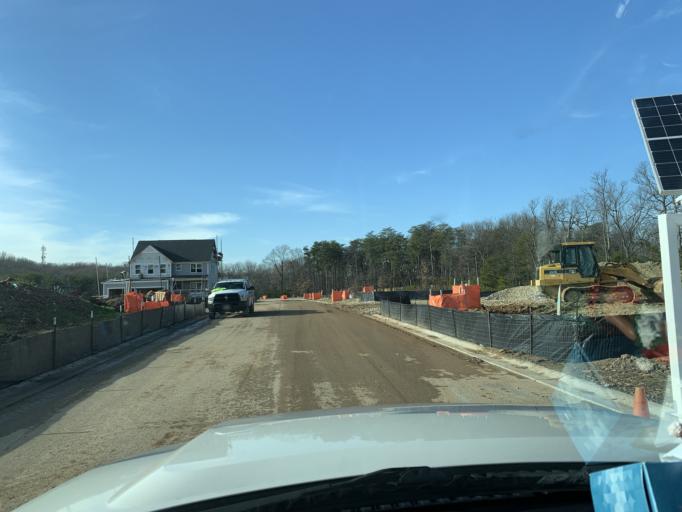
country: US
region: Maryland
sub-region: Anne Arundel County
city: Fort Meade
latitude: 39.1402
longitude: -76.7400
